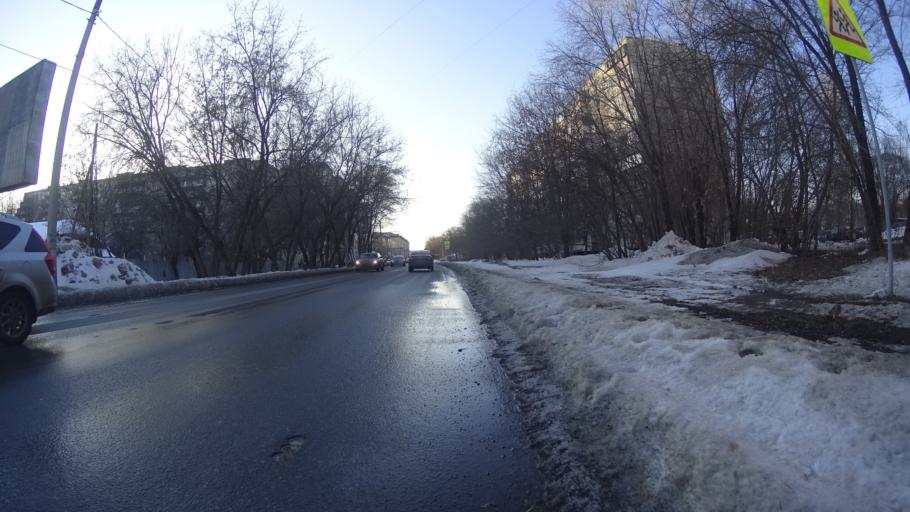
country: RU
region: Chelyabinsk
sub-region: Gorod Chelyabinsk
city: Chelyabinsk
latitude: 55.1380
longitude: 61.4468
